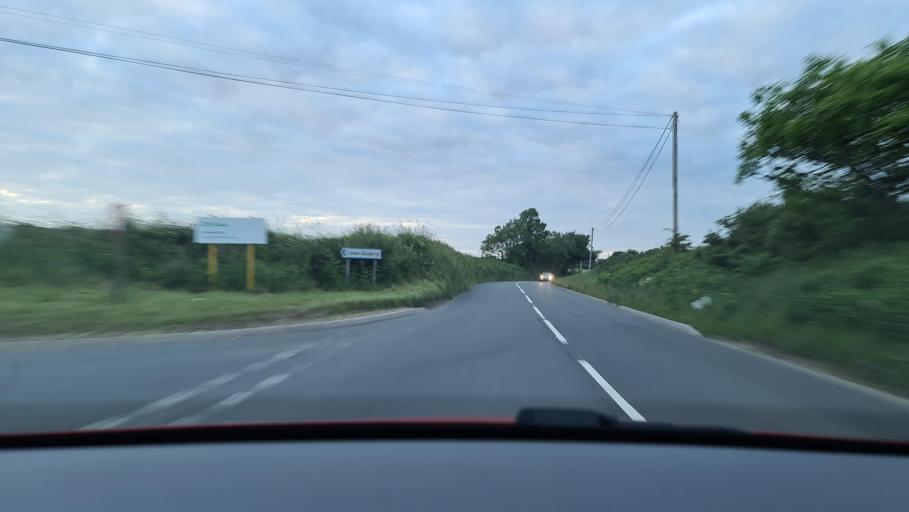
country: GB
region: England
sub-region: Cornwall
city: Liskeard
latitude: 50.4297
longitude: -4.4371
